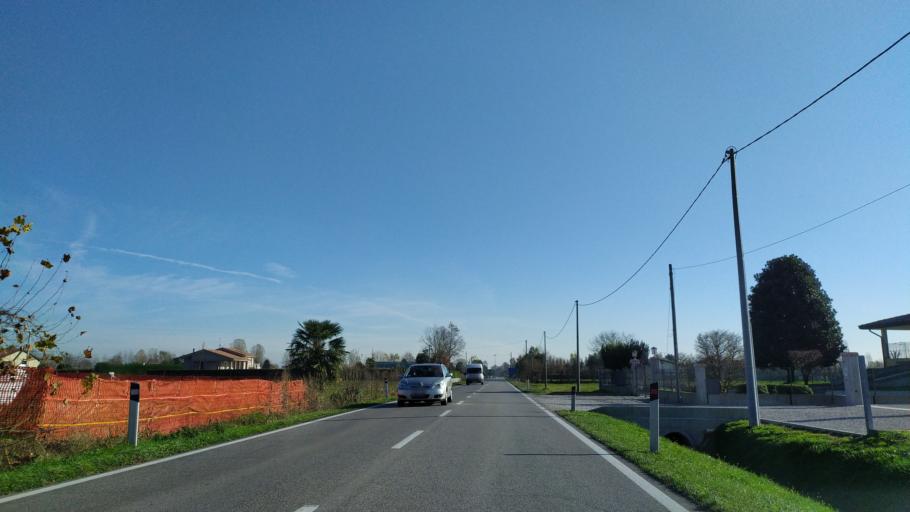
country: IT
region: Veneto
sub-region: Provincia di Padova
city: Villa del Conte
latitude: 45.5870
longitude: 11.8395
